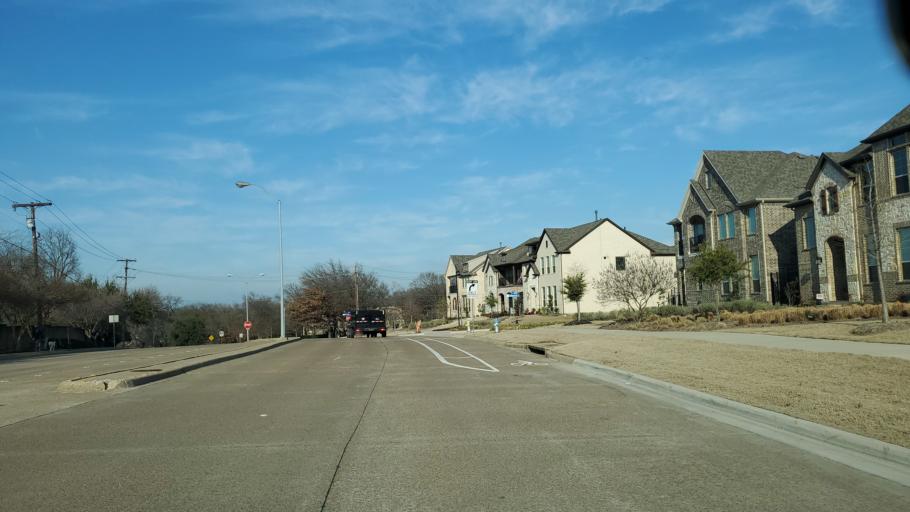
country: US
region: Texas
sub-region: Collin County
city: Plano
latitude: 32.9880
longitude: -96.7164
